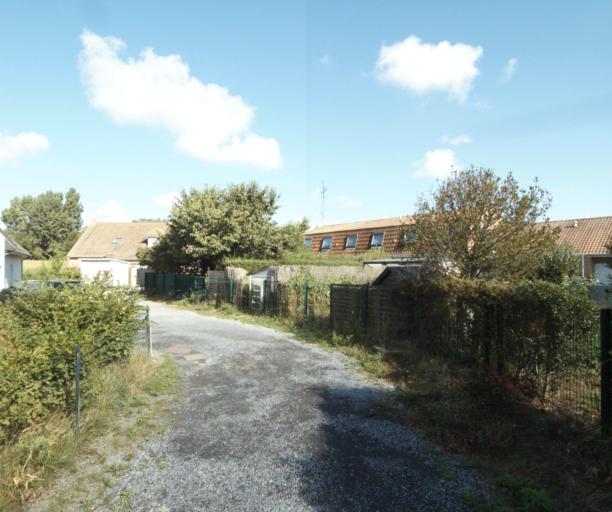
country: FR
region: Nord-Pas-de-Calais
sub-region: Departement du Nord
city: Sailly-lez-Lannoy
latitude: 50.6557
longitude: 3.2201
